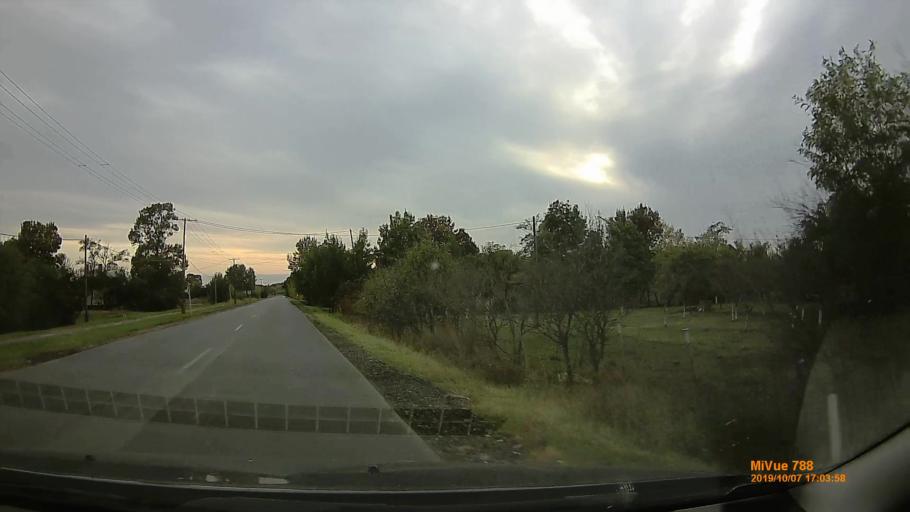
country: HU
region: Bekes
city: Szarvas
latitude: 46.8383
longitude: 20.5463
